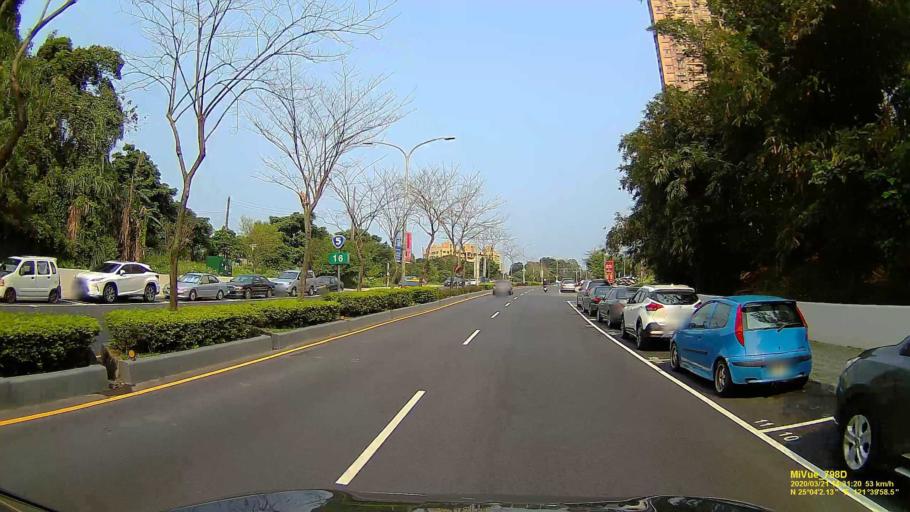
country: TW
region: Taiwan
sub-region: Keelung
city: Keelung
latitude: 25.0673
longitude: 121.6665
